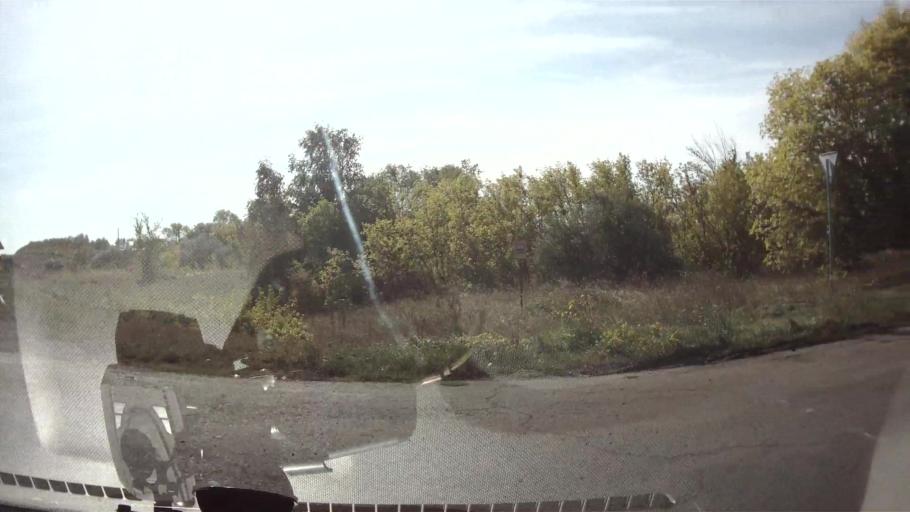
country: RU
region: Samara
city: Varlamovo
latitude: 53.3336
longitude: 48.4248
